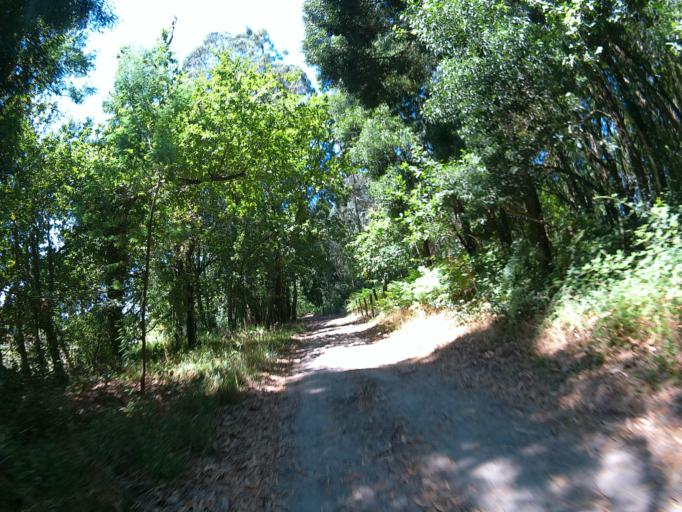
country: PT
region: Viana do Castelo
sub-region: Viana do Castelo
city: Darque
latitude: 41.7107
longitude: -8.7181
